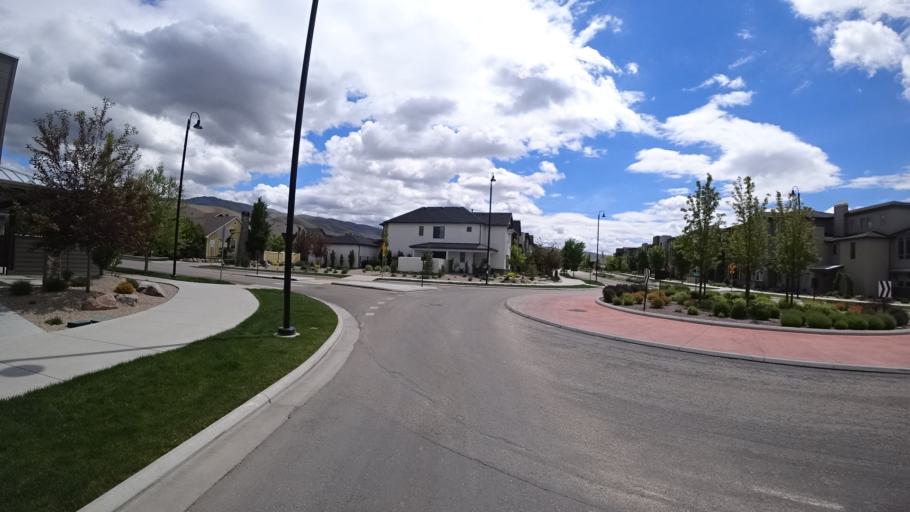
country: US
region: Idaho
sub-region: Ada County
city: Boise
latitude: 43.5759
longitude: -116.1378
